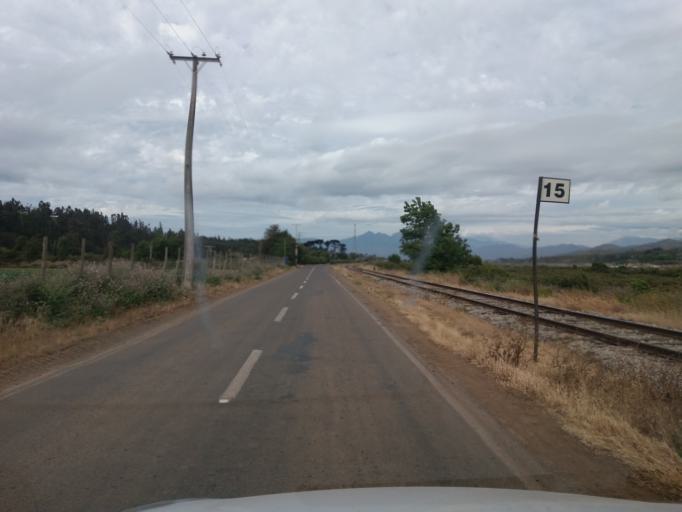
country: CL
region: Valparaiso
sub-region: Provincia de Marga Marga
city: Villa Alemana
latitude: -32.9166
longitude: -71.4093
